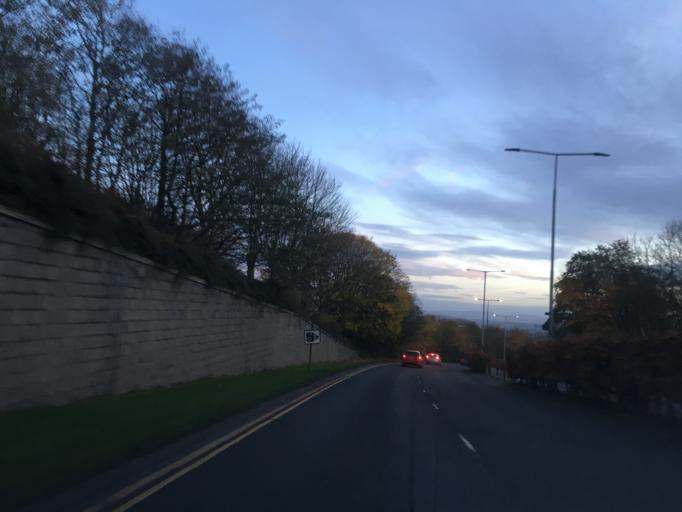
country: GB
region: Scotland
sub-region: Fife
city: Dunfermline
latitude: 56.0723
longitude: -3.4519
